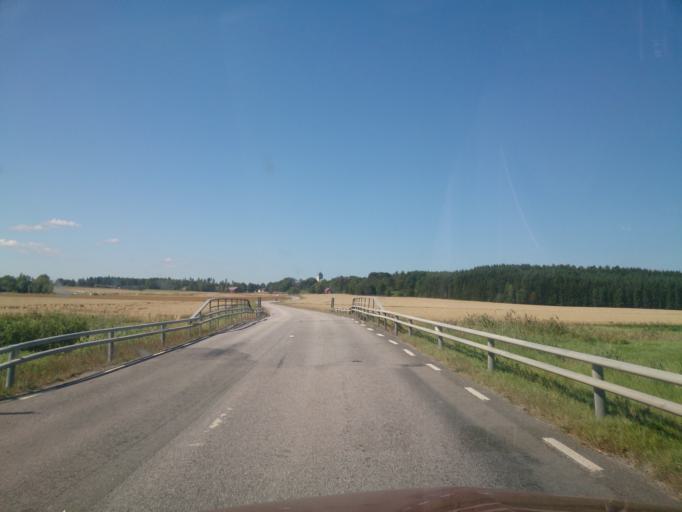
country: SE
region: OEstergoetland
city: Lindo
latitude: 58.5806
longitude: 16.3355
